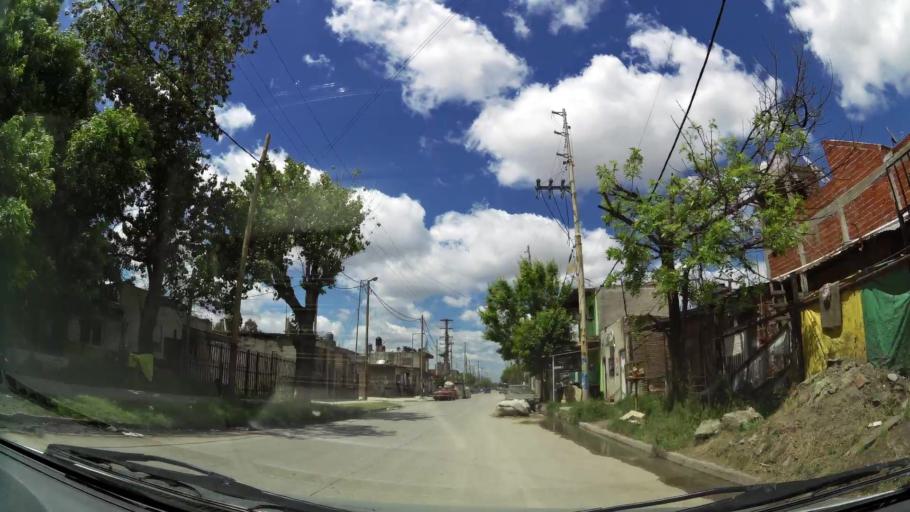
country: AR
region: Buenos Aires F.D.
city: Villa Lugano
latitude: -34.6935
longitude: -58.4434
